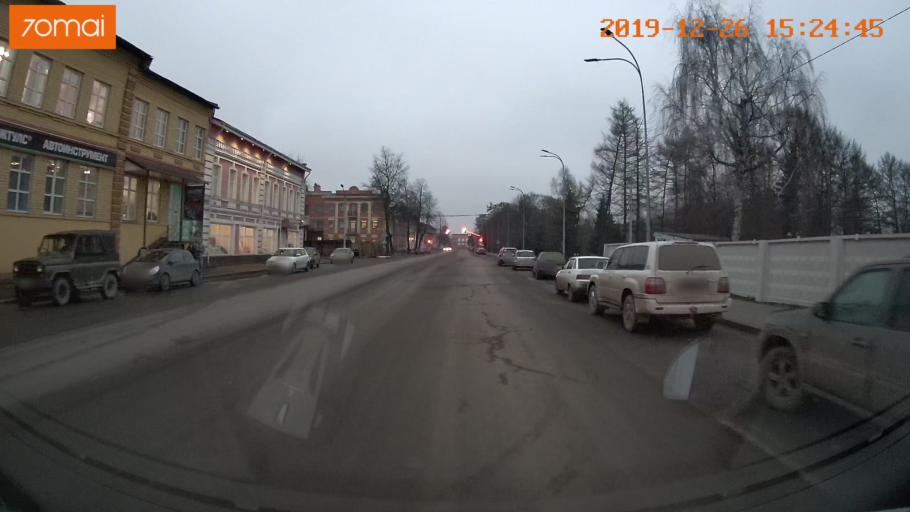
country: RU
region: Jaroslavl
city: Rybinsk
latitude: 58.0514
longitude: 38.8454
